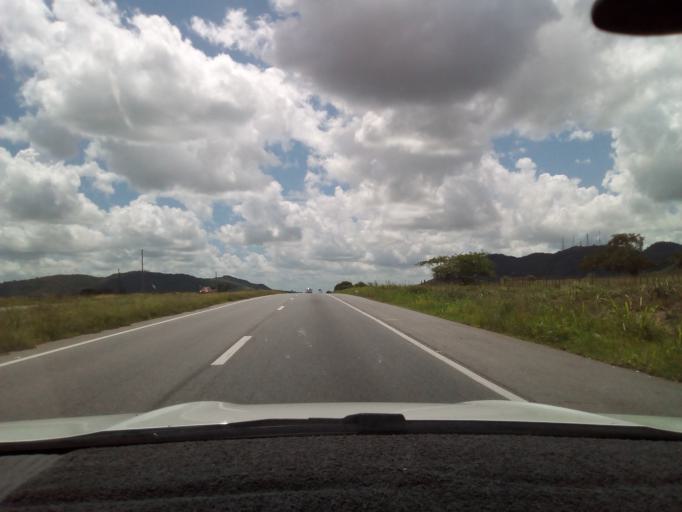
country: BR
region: Paraiba
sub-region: Gurinhem
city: Gurinhem
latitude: -7.1828
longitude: -35.4376
